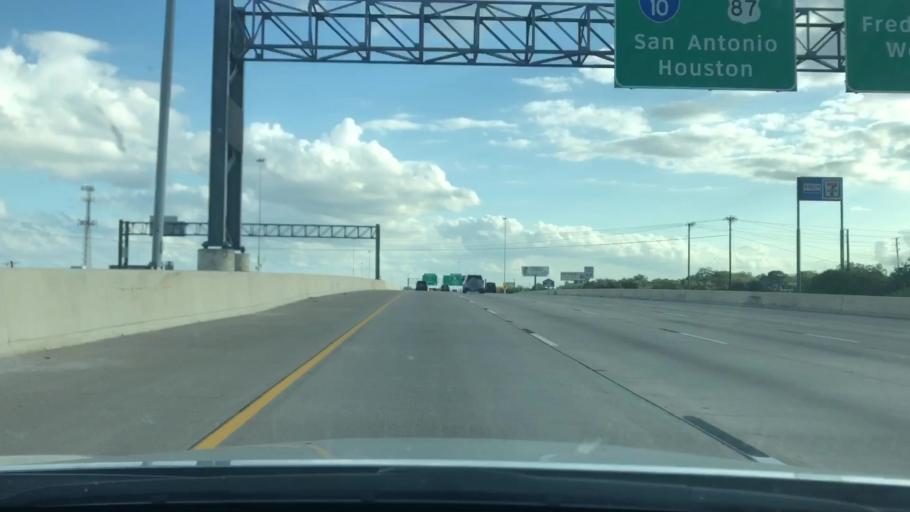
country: US
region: Texas
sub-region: Bexar County
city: Olmos Park
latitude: 29.4678
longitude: -98.5160
